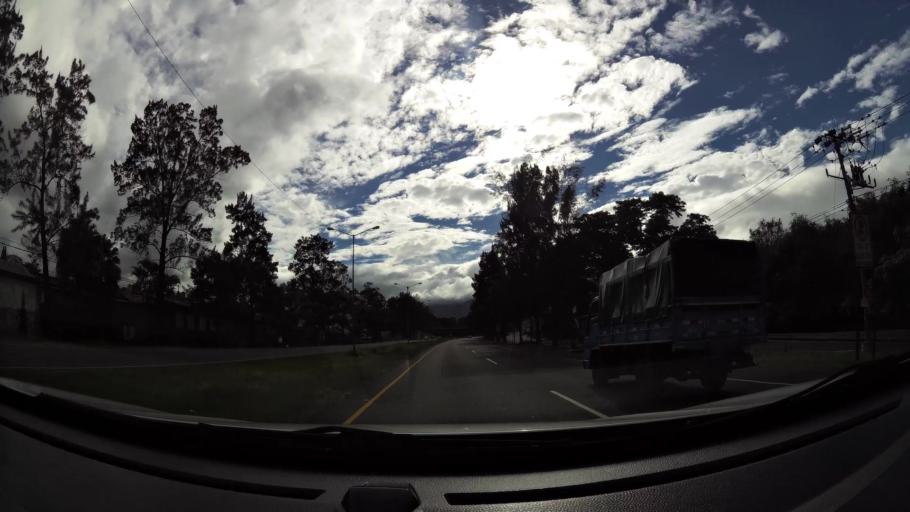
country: CR
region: San Jose
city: Curridabat
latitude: 9.9109
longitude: -84.0202
